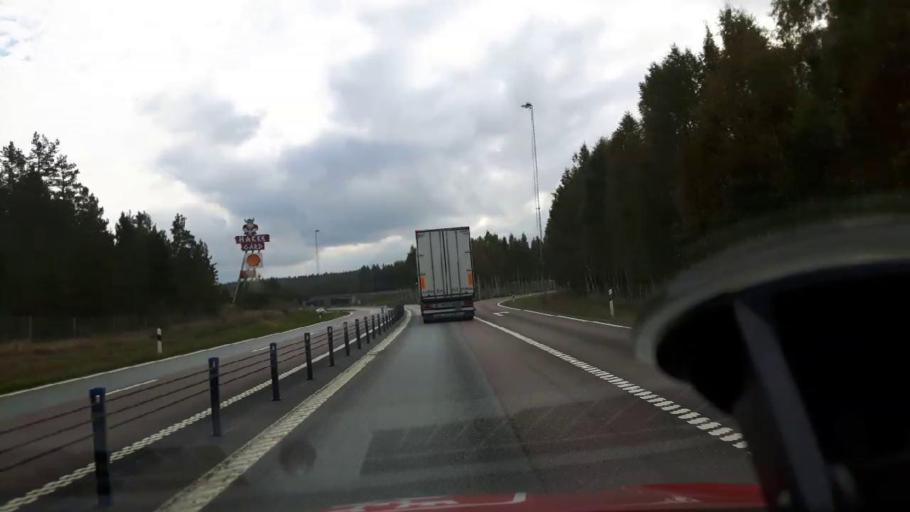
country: SE
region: Gaevleborg
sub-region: Gavle Kommun
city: Norrsundet
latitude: 60.9058
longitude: 17.0151
